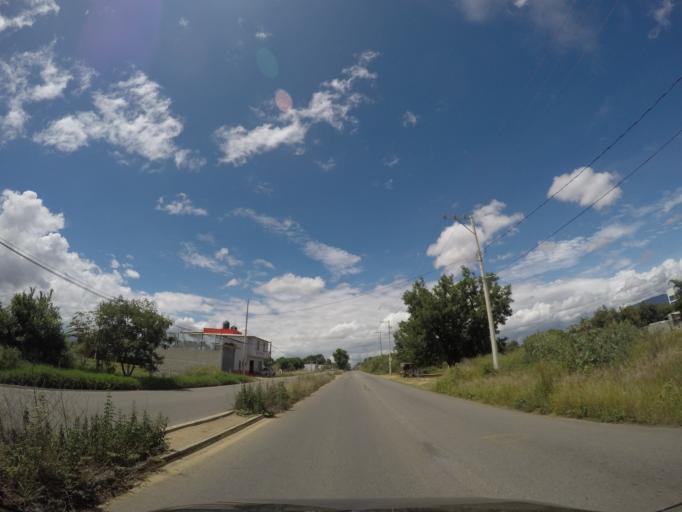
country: MX
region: Oaxaca
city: San Raymundo Jalpam
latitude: 16.9760
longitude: -96.7498
